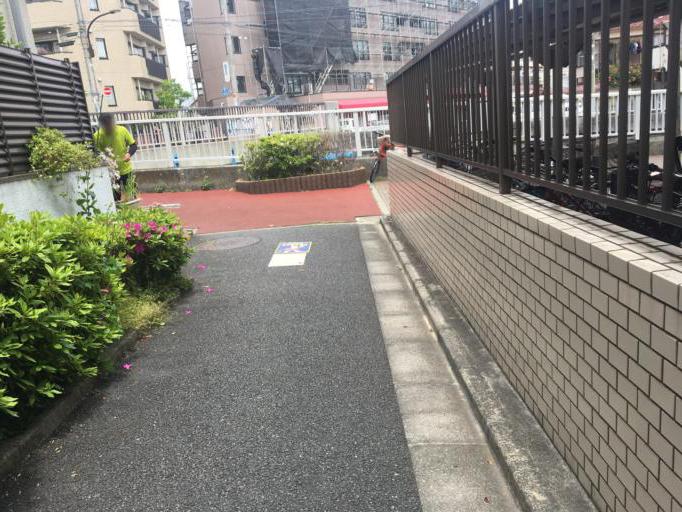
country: JP
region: Saitama
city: Wako
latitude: 35.7489
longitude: 139.6635
